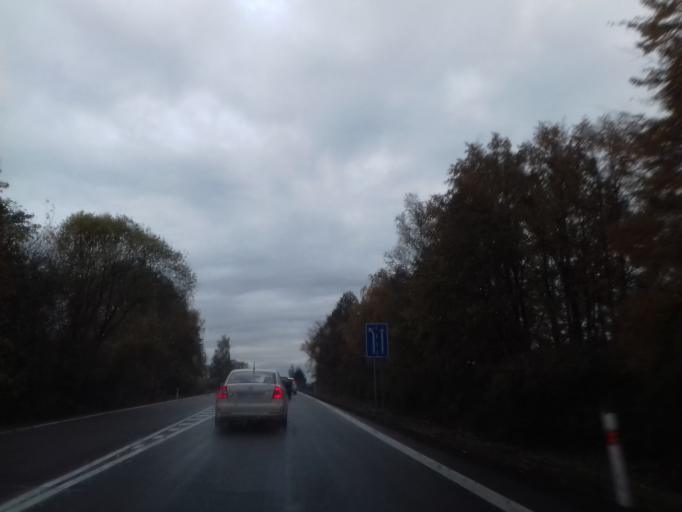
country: CZ
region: Pardubicky
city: Horni Jeleni
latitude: 50.0032
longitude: 16.0991
